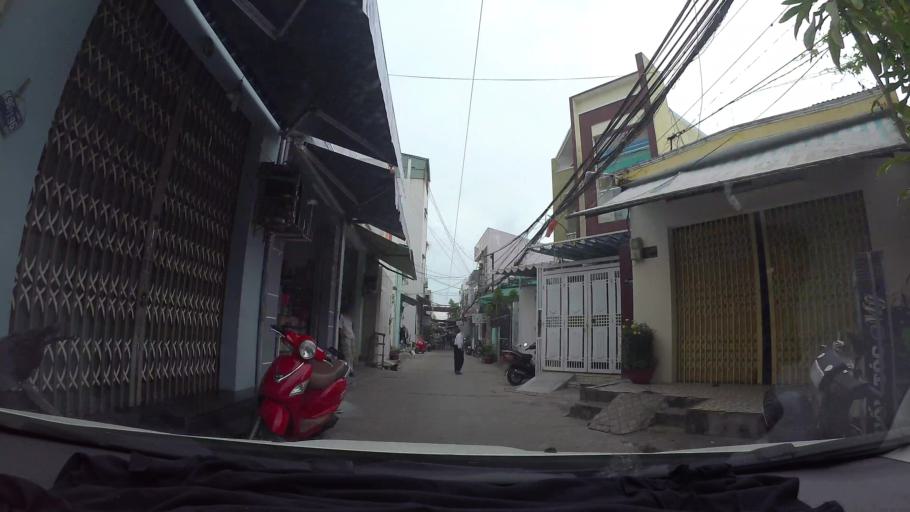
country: VN
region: Da Nang
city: Thanh Khe
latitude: 16.0676
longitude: 108.1952
